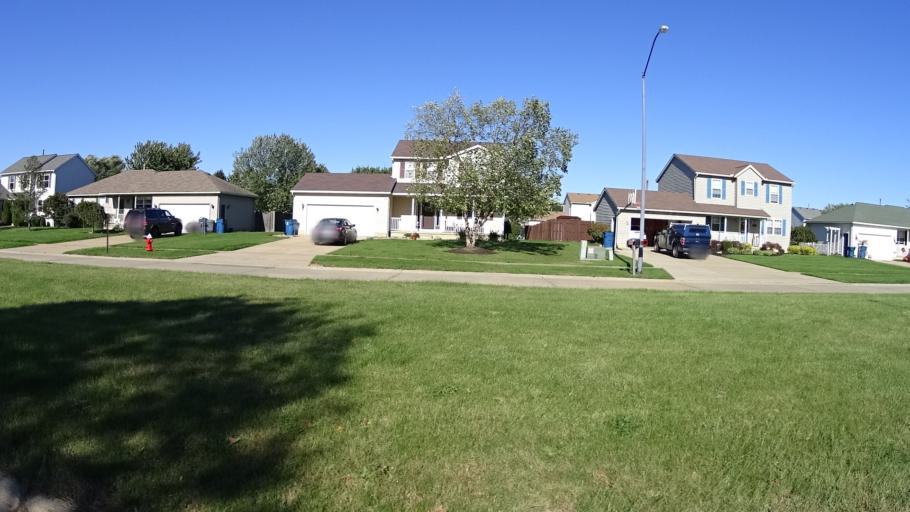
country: US
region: Ohio
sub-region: Lorain County
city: Amherst
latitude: 41.4194
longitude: -82.2165
